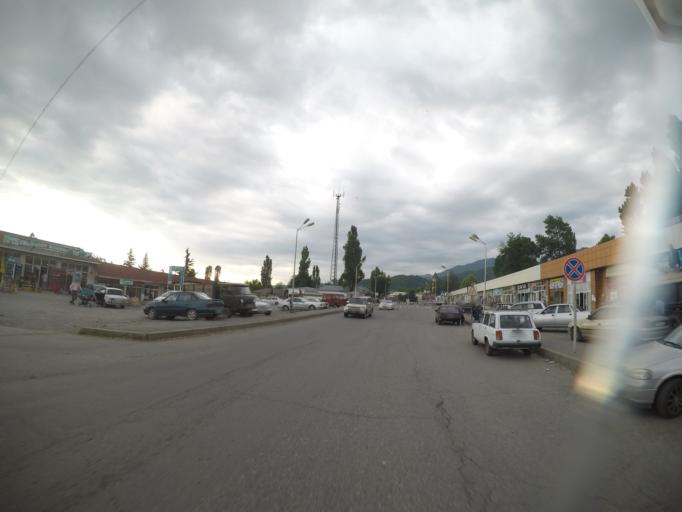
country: AZ
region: Qabala Rayon
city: Qutqashen
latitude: 40.9457
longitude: 47.9431
